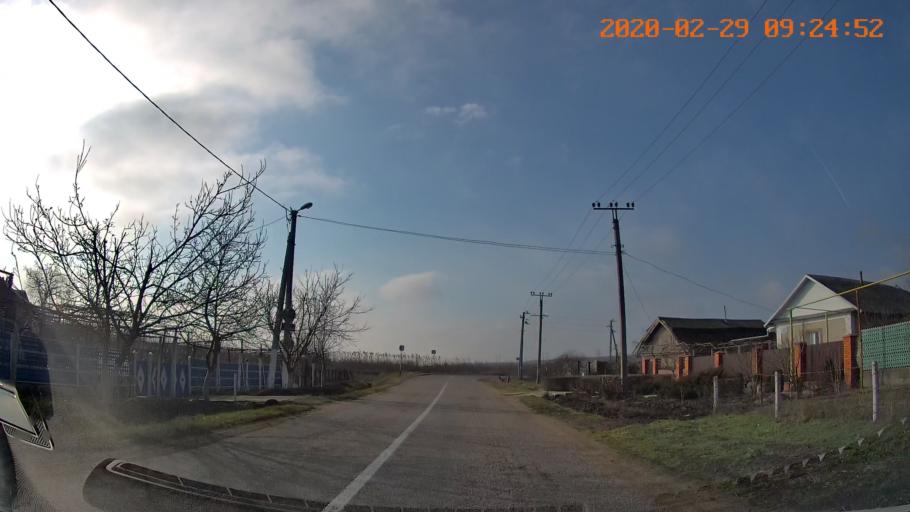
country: MD
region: Telenesti
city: Pervomaisc
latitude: 46.7119
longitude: 29.9574
